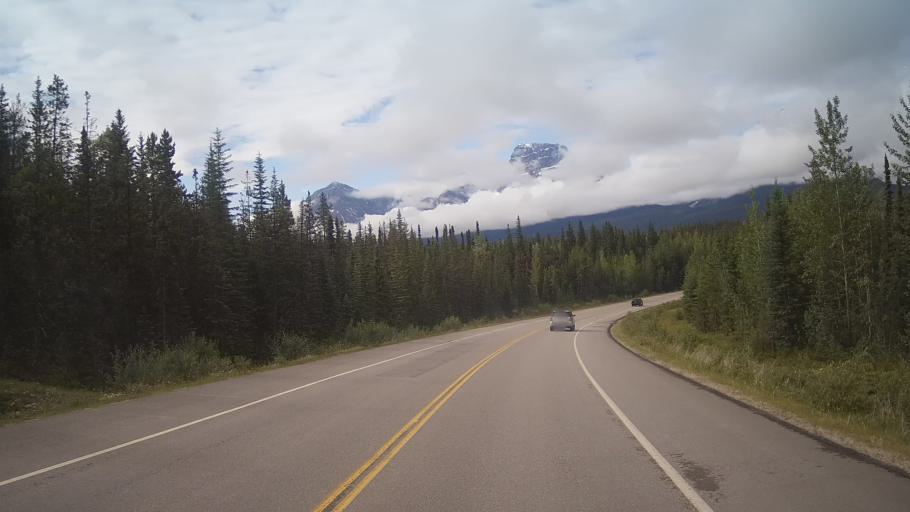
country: CA
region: Alberta
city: Jasper Park Lodge
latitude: 52.6846
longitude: -117.8659
